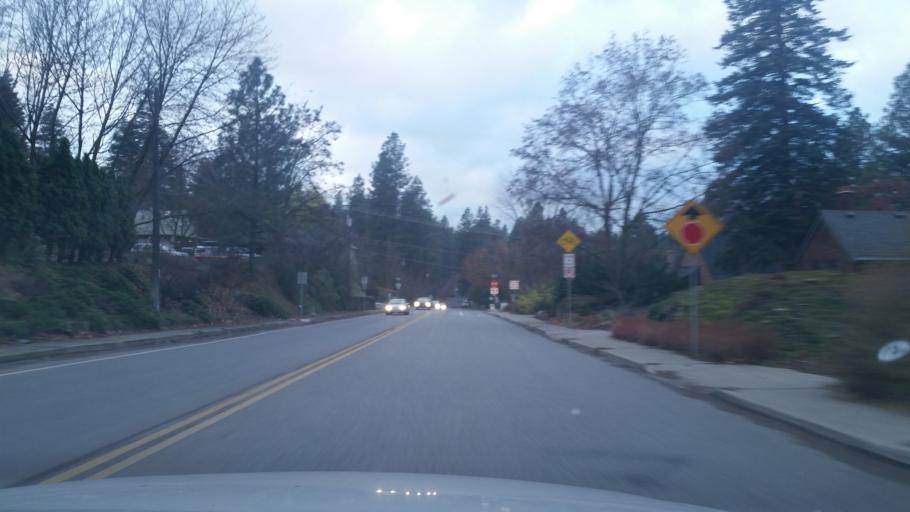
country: US
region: Washington
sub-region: Spokane County
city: Spokane
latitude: 47.6389
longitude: -117.3886
